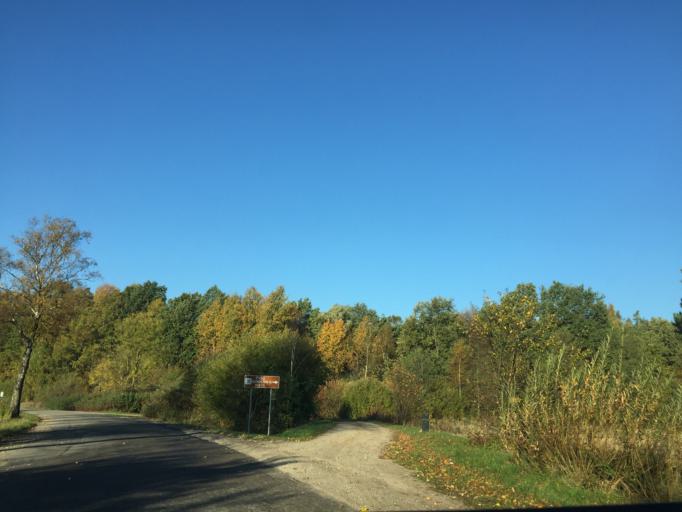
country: LT
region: Klaipedos apskritis
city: Kretinga
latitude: 55.8928
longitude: 21.2105
